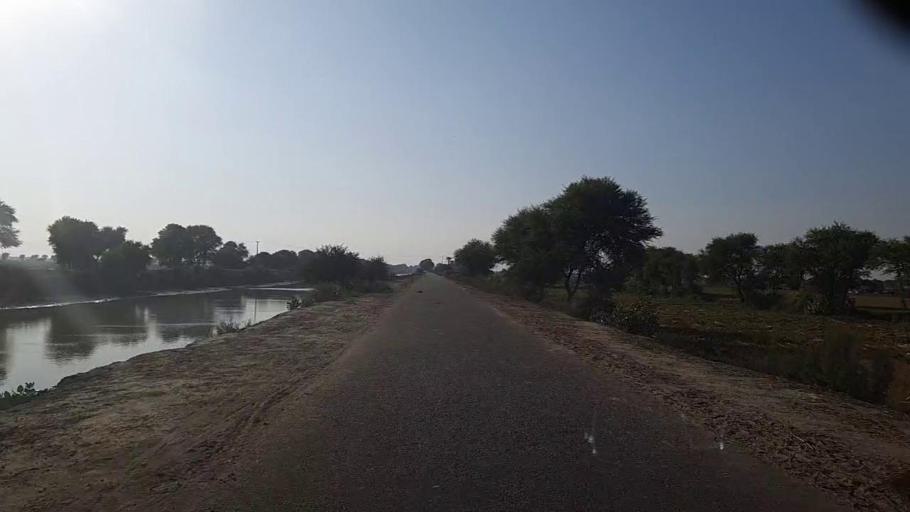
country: PK
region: Sindh
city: Tangwani
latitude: 28.3012
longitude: 68.9392
